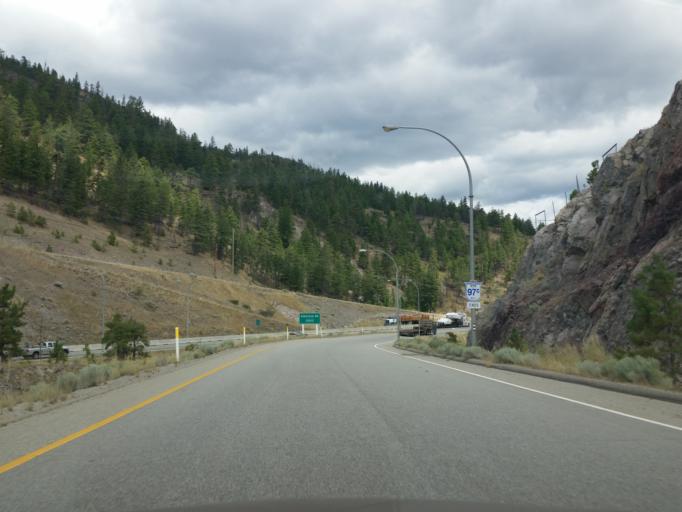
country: CA
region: British Columbia
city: Peachland
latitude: 49.8075
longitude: -119.6613
